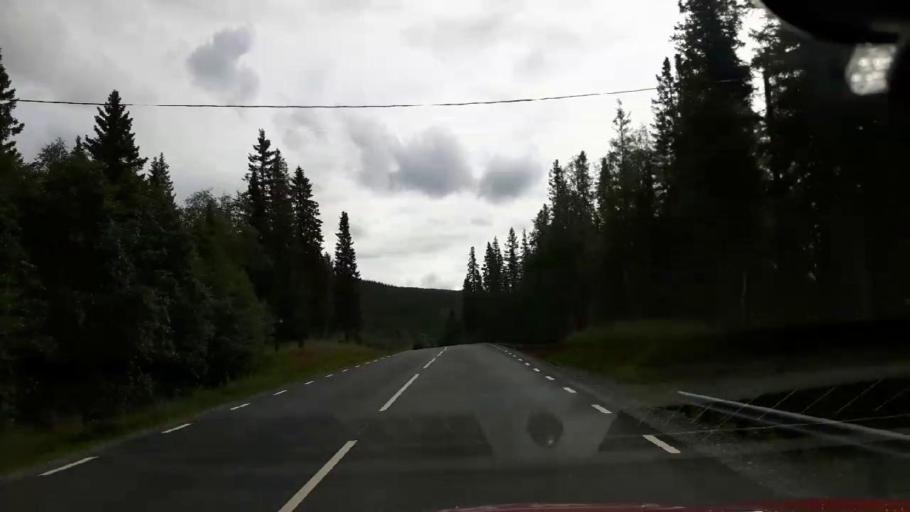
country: NO
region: Nord-Trondelag
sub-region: Lierne
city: Sandvika
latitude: 64.6476
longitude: 14.1398
